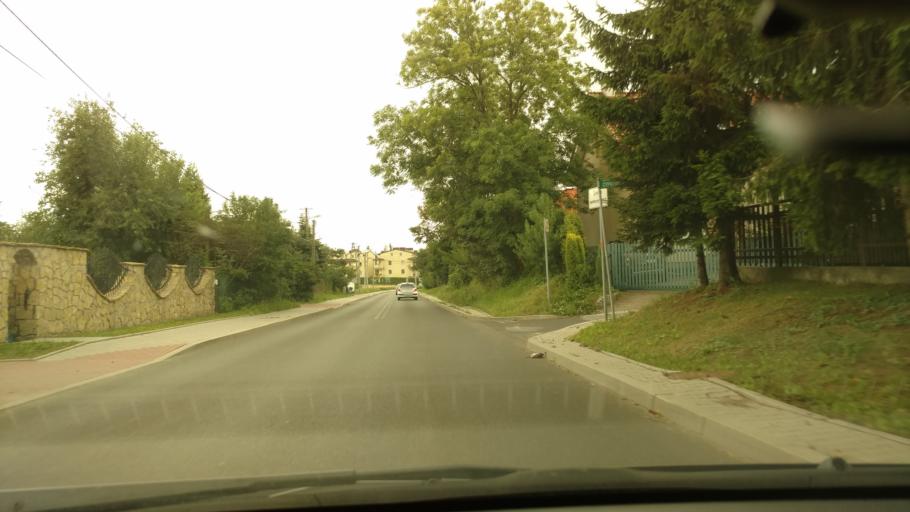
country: PL
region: Lesser Poland Voivodeship
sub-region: Powiat krakowski
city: Zielonki
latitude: 50.1208
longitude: 19.9403
